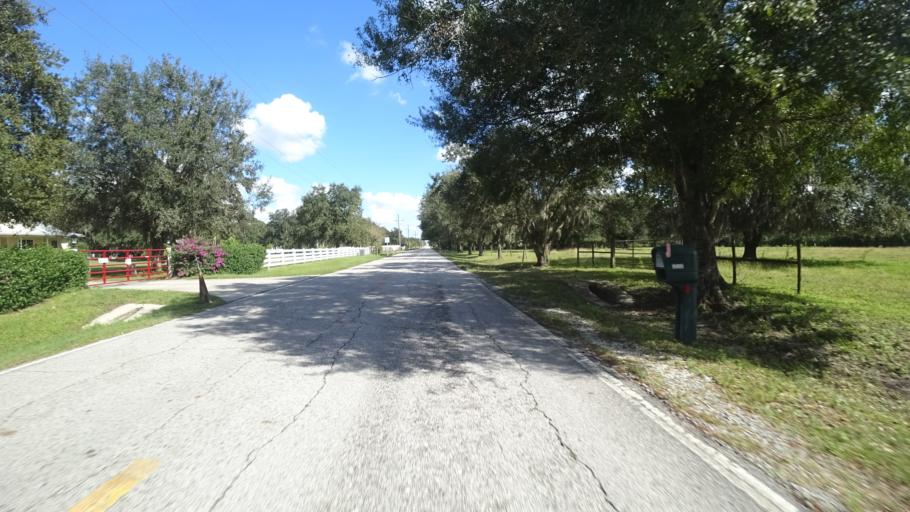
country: US
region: Florida
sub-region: Manatee County
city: Ellenton
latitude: 27.4878
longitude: -82.3826
